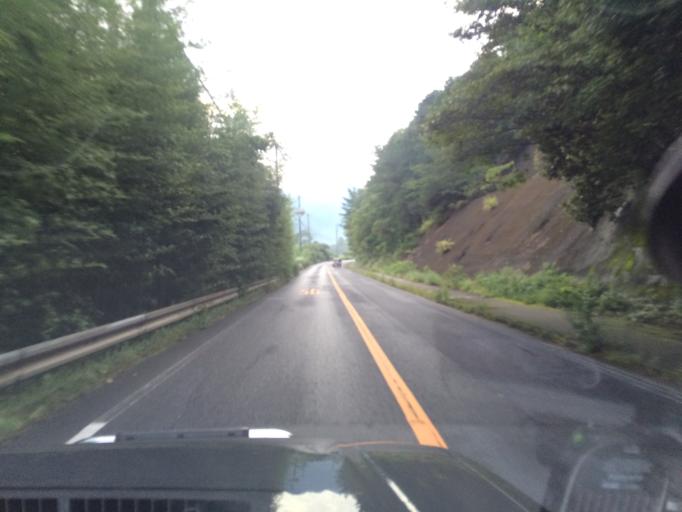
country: JP
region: Hyogo
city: Nishiwaki
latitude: 35.0945
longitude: 134.9974
